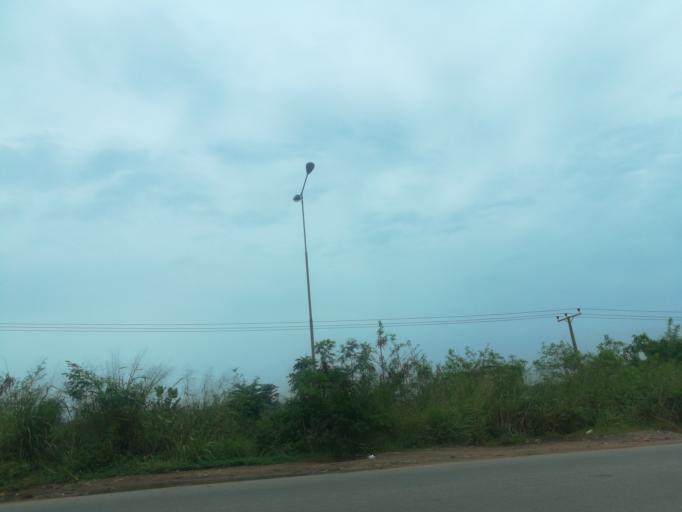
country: NG
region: Oyo
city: Egbeda
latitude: 7.3834
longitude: 3.9921
